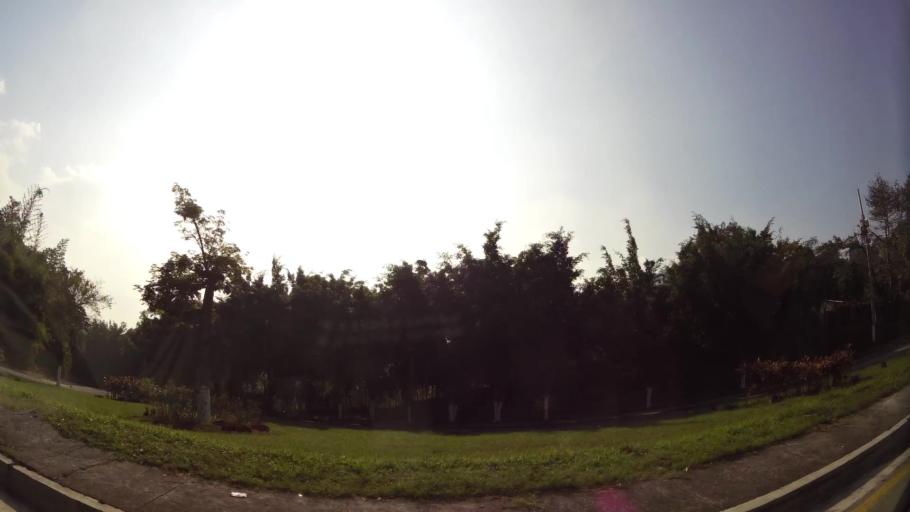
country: SV
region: San Salvador
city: San Salvador
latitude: 13.6781
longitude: -89.2170
